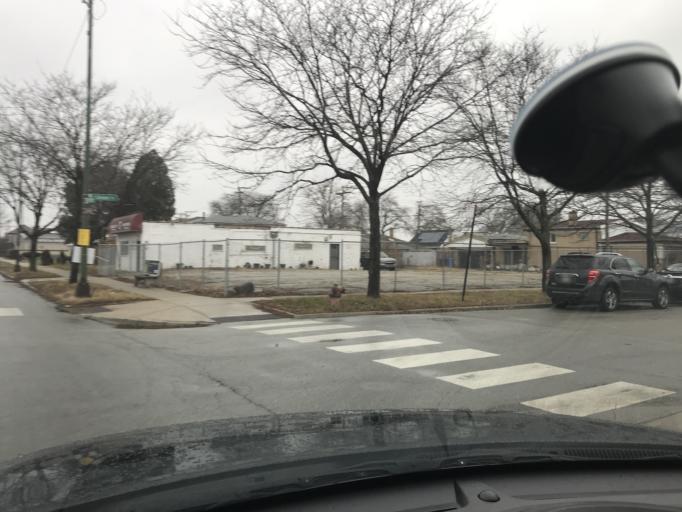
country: US
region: Illinois
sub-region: Cook County
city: Evergreen Park
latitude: 41.7216
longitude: -87.6406
